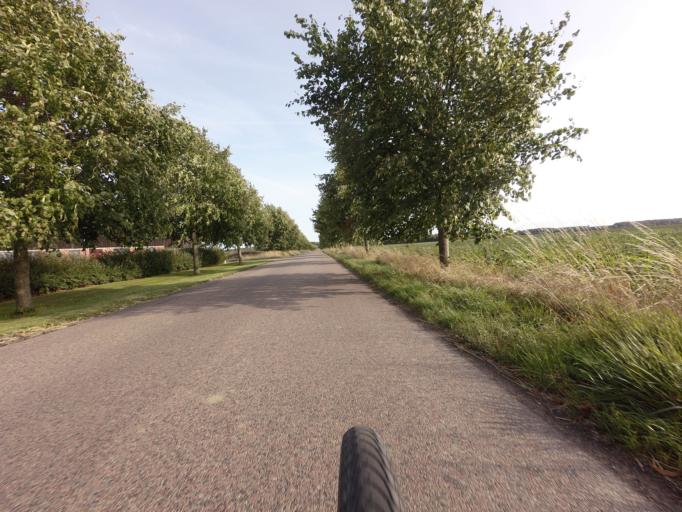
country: DK
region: Zealand
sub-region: Faxe Kommune
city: Fakse Ladeplads
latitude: 55.2521
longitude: 12.2257
